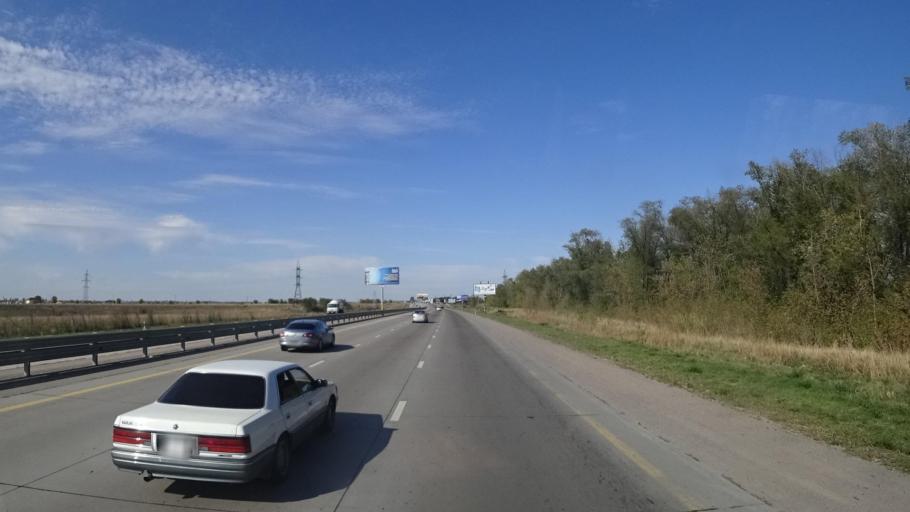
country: KZ
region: Almaty Oblysy
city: Energeticheskiy
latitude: 43.4214
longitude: 76.9856
